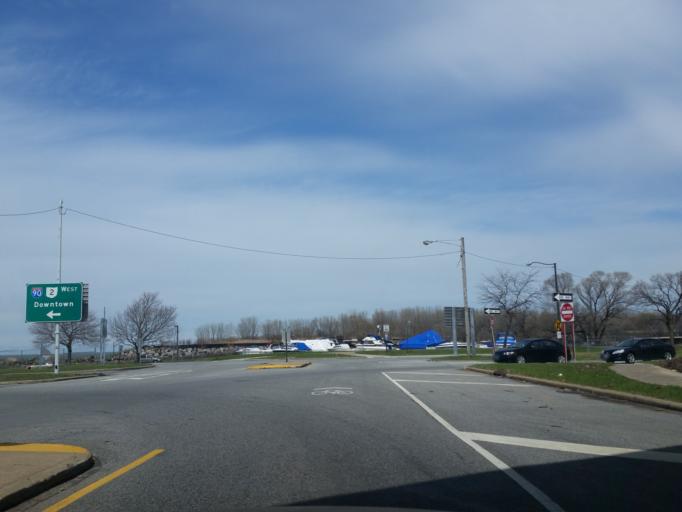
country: US
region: Ohio
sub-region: Cuyahoga County
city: Bratenahl
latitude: 41.5389
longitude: -81.6382
